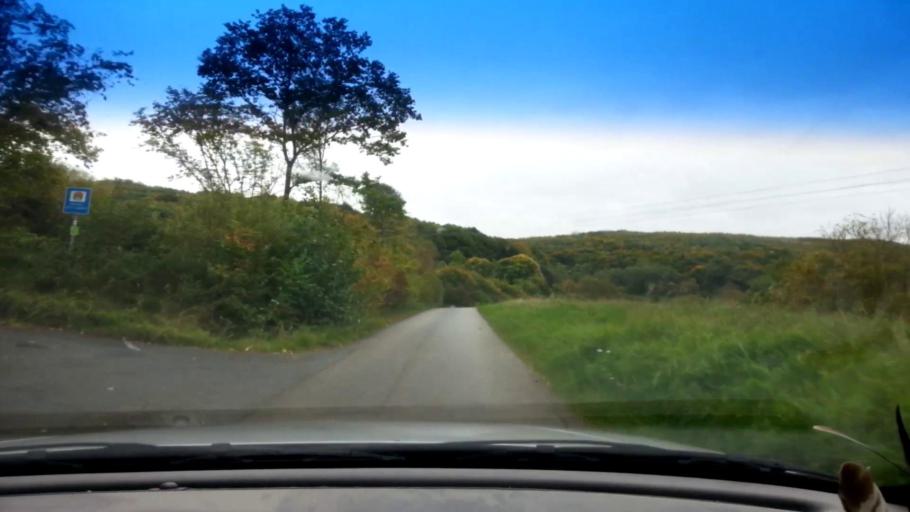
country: DE
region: Bavaria
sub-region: Upper Franconia
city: Litzendorf
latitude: 49.9003
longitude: 11.0413
